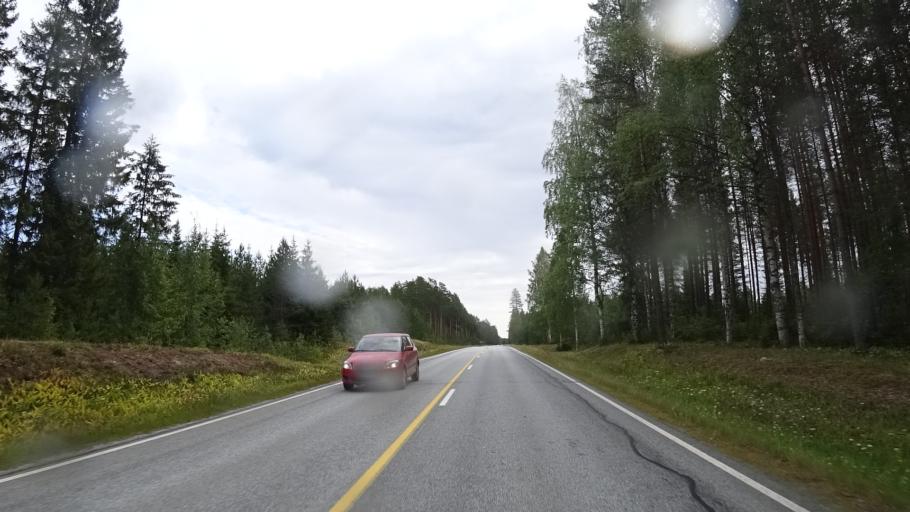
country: FI
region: North Karelia
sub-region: Keski-Karjala
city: Raeaekkylae
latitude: 62.1106
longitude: 29.7237
